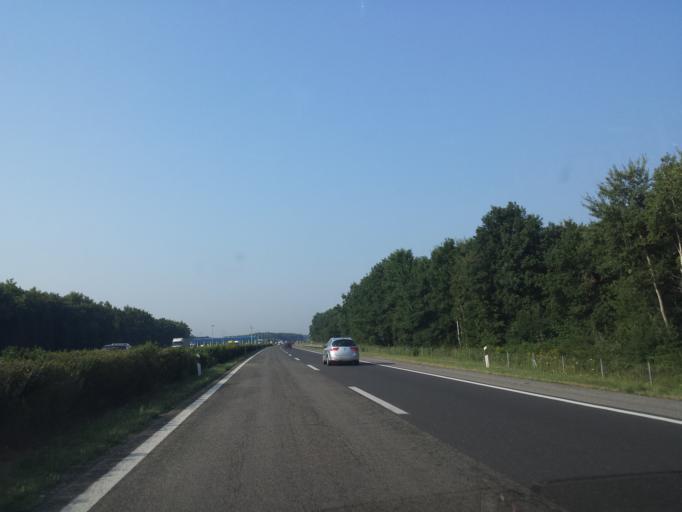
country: HR
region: Grad Zagreb
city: Brezovica
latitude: 45.7286
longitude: 15.8730
